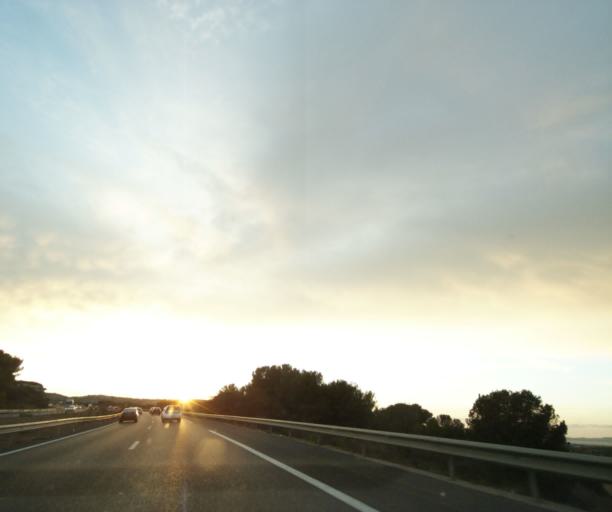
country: FR
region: Provence-Alpes-Cote d'Azur
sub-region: Departement des Bouches-du-Rhone
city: Ensues-la-Redonne
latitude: 43.3802
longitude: 5.2070
